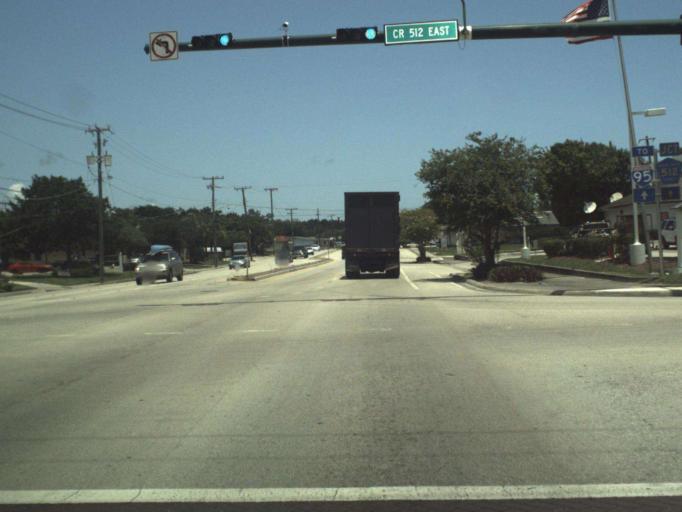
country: US
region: Florida
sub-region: Indian River County
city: Sebastian
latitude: 27.8088
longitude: -80.4662
